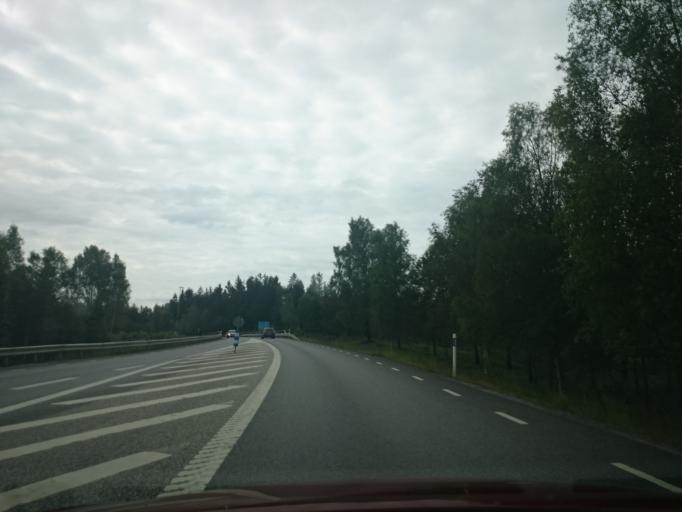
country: SE
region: Vaestra Goetaland
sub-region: Harryda Kommun
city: Hindas
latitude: 57.6756
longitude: 12.3534
